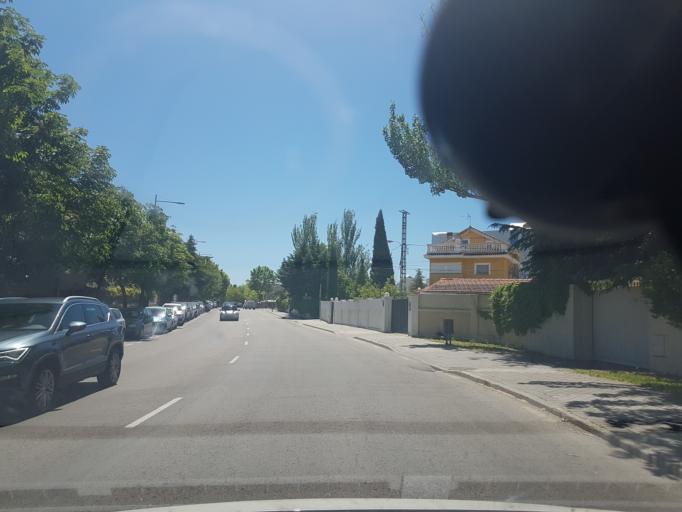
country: ES
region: Madrid
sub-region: Provincia de Madrid
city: Pozuelo de Alarcon
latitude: 40.4380
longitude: -3.8010
